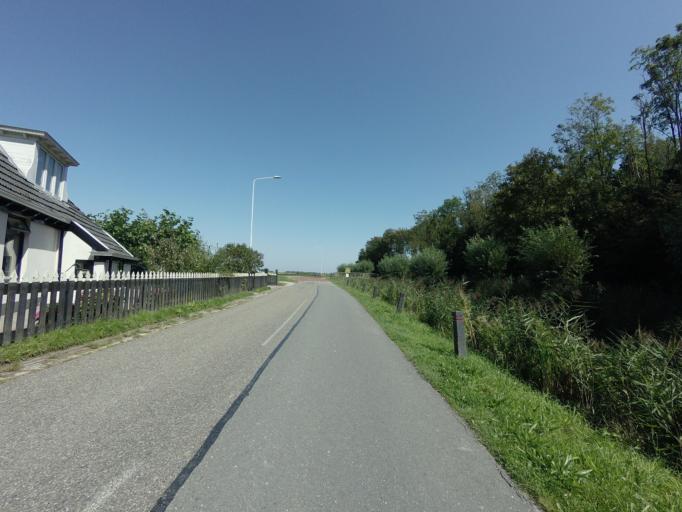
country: NL
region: Friesland
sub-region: Gemeente Dongeradeel
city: Anjum
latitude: 53.3820
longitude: 6.0552
